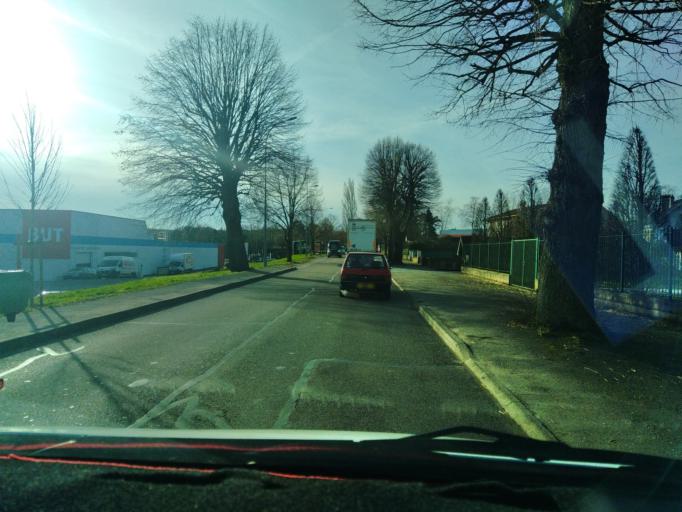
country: FR
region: Franche-Comte
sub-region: Departement de la Haute-Saone
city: Gray
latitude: 47.4378
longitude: 5.5995
